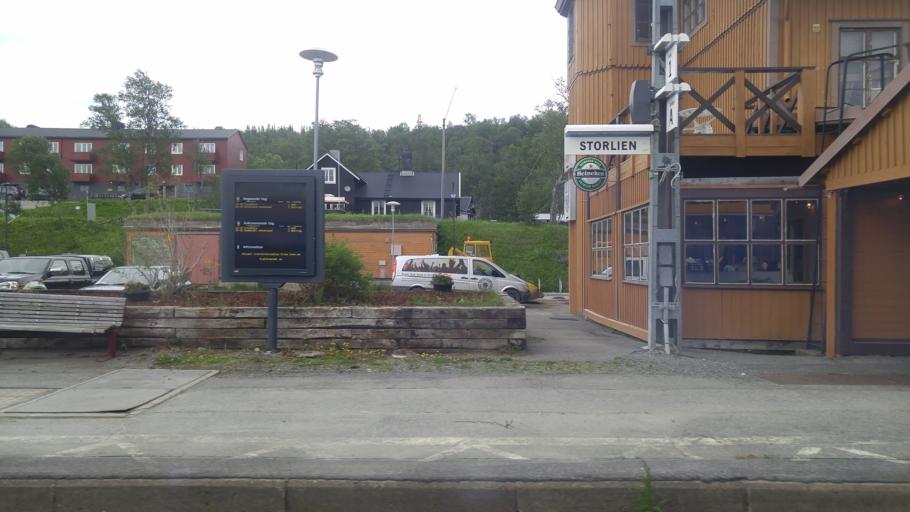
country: NO
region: Nord-Trondelag
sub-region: Meraker
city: Meraker
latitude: 63.3159
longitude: 12.1007
